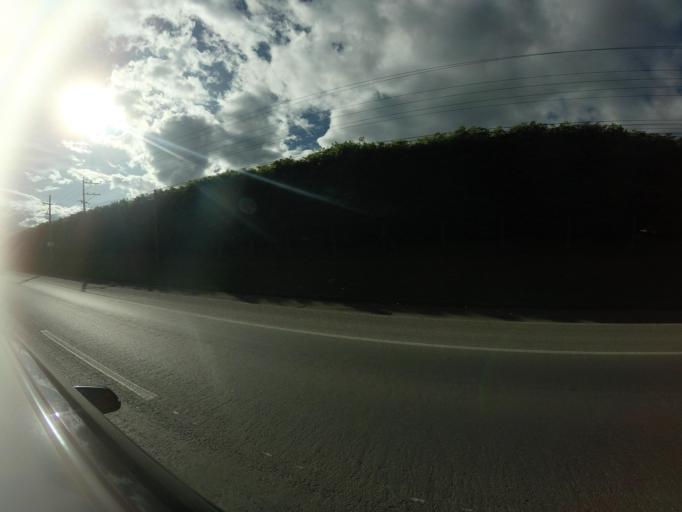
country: CO
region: Cundinamarca
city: Sopo
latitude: 4.9392
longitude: -73.9742
